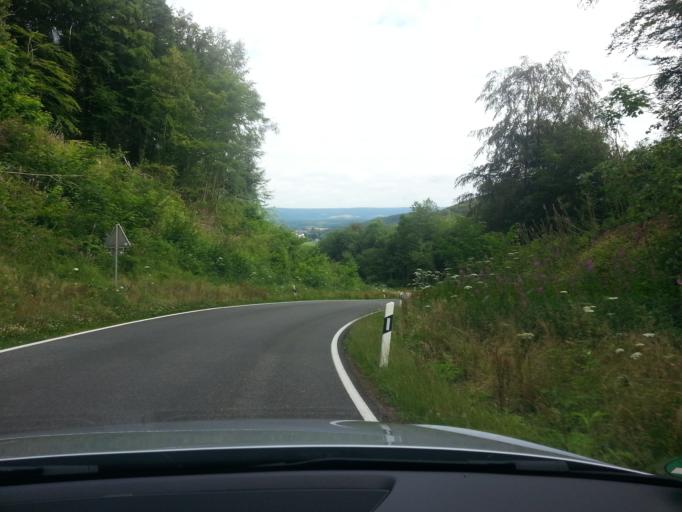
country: DE
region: Saarland
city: Losheim
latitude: 49.4732
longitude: 6.7920
